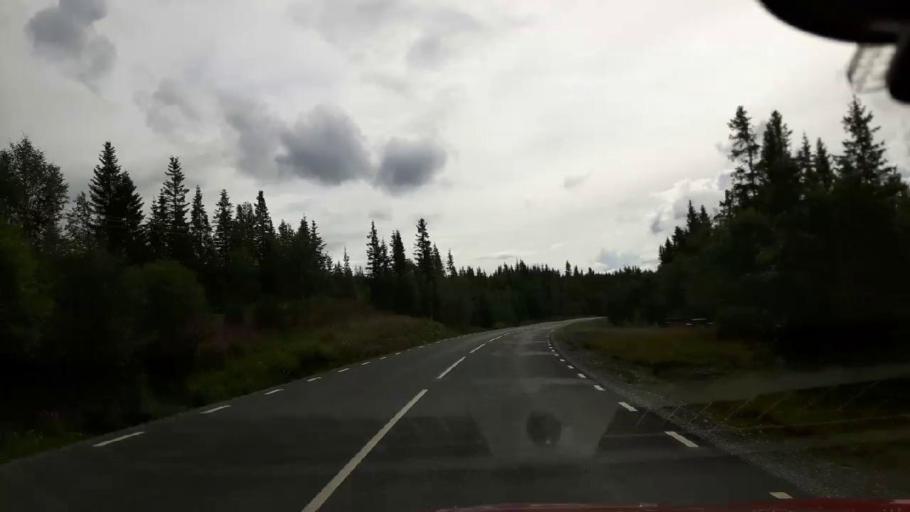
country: NO
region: Nord-Trondelag
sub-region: Lierne
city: Sandvika
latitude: 64.6453
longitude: 14.1422
